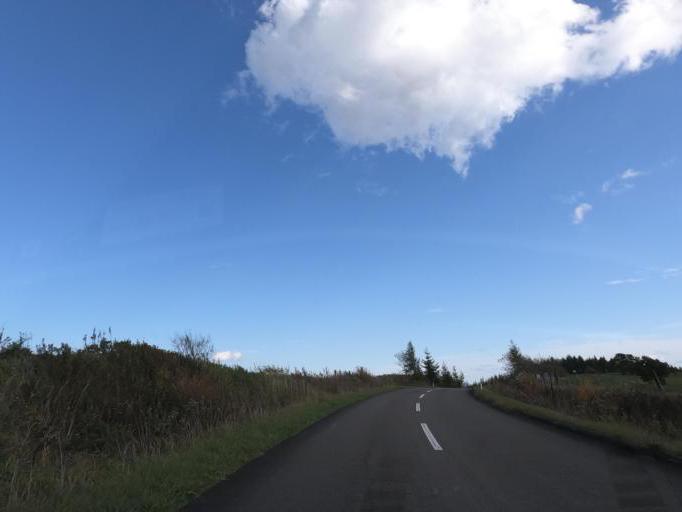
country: JP
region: Hokkaido
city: Otofuke
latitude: 43.2773
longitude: 143.2337
